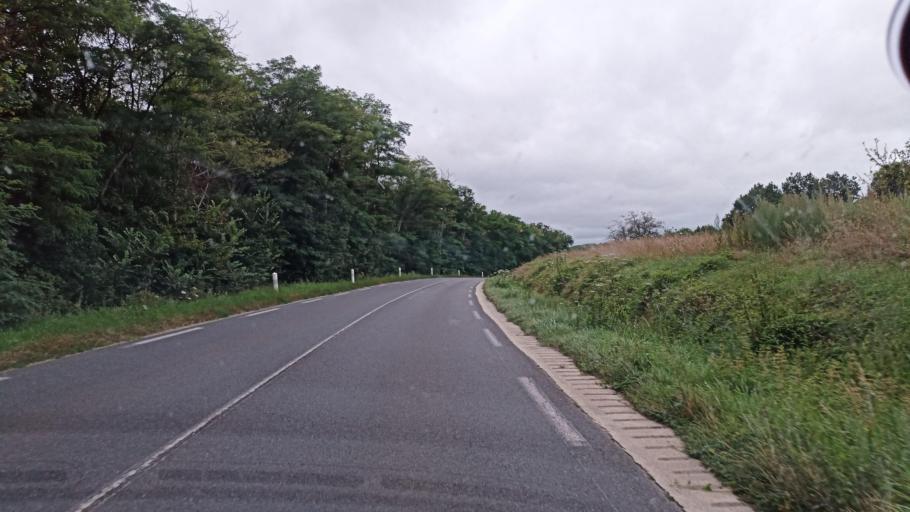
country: FR
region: Ile-de-France
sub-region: Departement de Seine-et-Marne
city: Voulx
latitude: 48.2902
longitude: 2.9522
